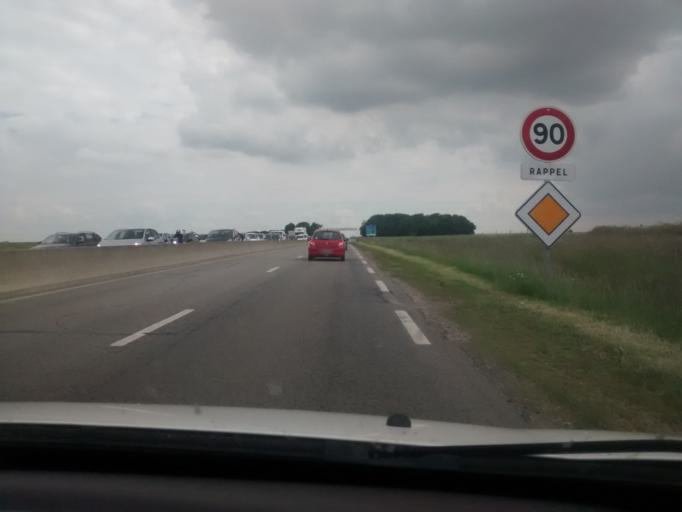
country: FR
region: Ile-de-France
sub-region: Departement des Yvelines
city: Rambouillet
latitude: 48.6151
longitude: 1.8313
